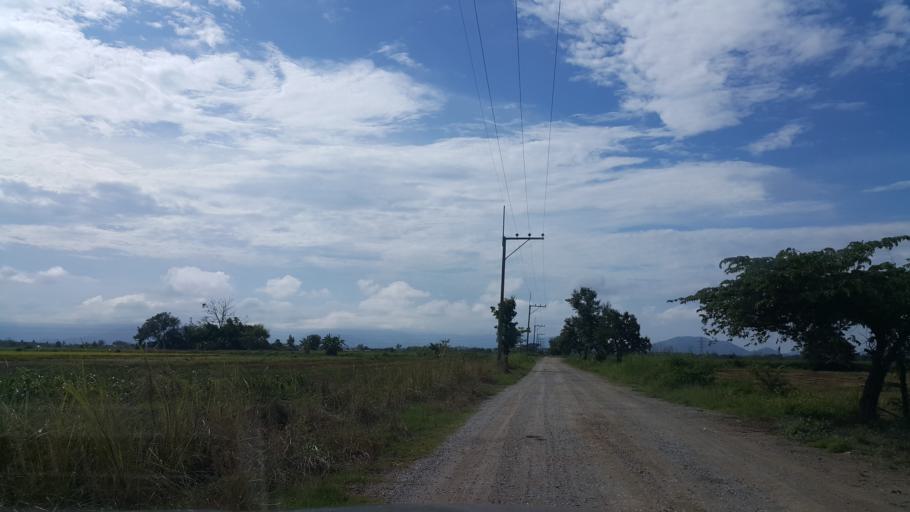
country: TH
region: Chiang Rai
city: Wiang Chai
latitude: 19.9532
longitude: 99.9300
